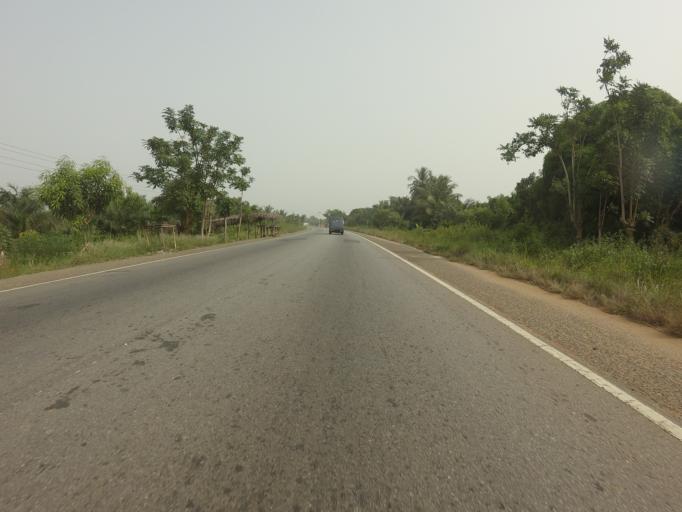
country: GH
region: Volta
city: Anloga
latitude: 5.9925
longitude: 0.5688
